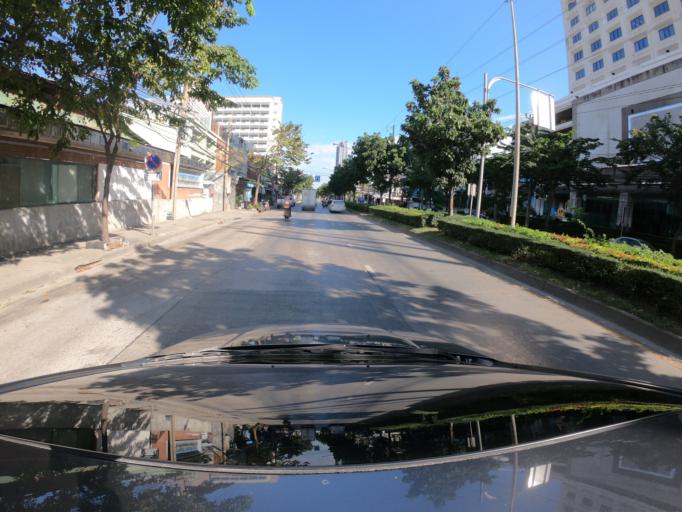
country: TH
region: Bangkok
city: Phra Khanong
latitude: 13.6746
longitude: 100.5995
